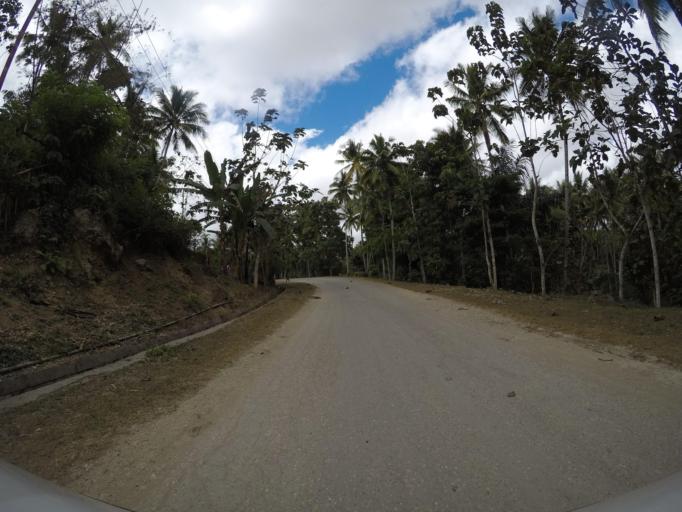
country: TL
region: Lautem
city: Lospalos
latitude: -8.4403
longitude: 126.9711
